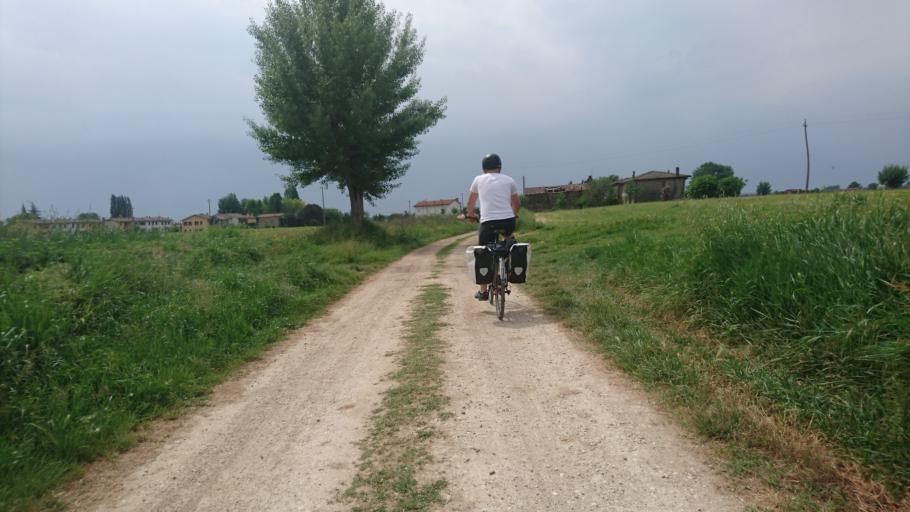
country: IT
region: Veneto
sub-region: Provincia di Padova
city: Monselice
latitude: 45.2185
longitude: 11.7311
